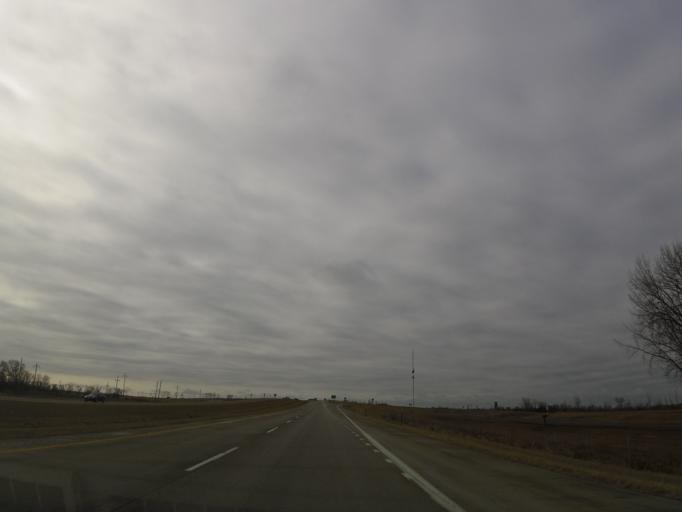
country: US
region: North Dakota
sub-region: Walsh County
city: Grafton
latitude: 48.2023
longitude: -97.1893
